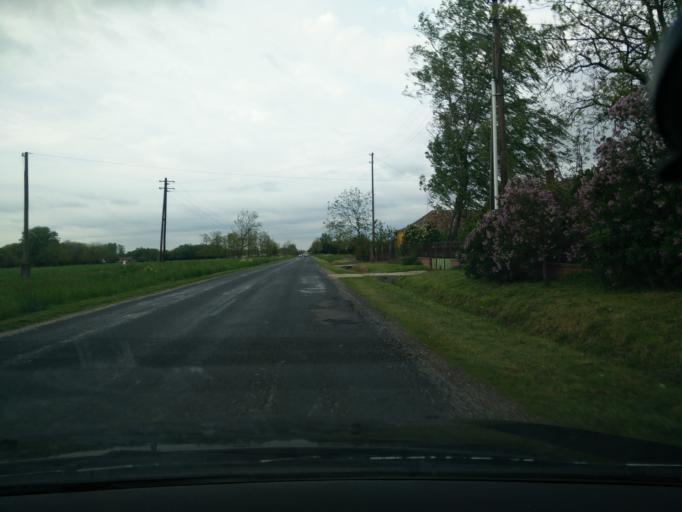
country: HU
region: Veszprem
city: Papa
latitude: 47.2745
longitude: 17.4148
